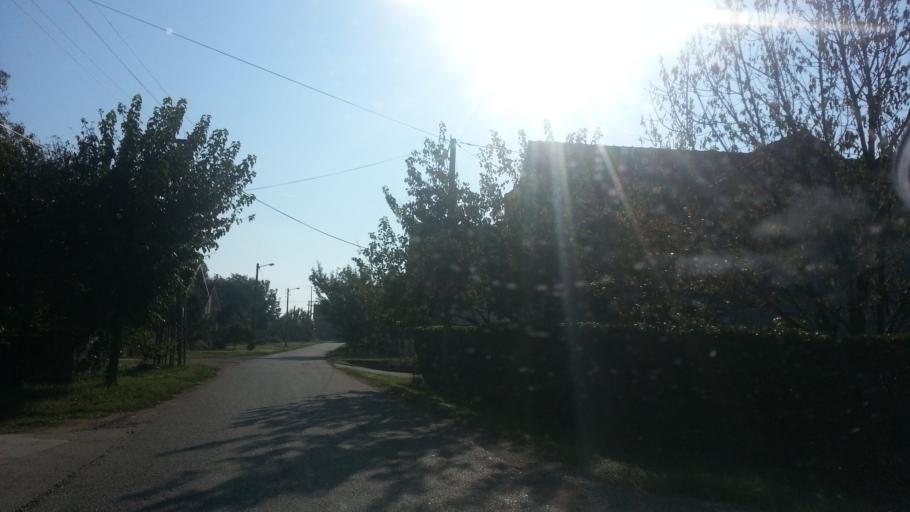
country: RS
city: Stari Banovci
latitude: 44.9824
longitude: 20.2709
